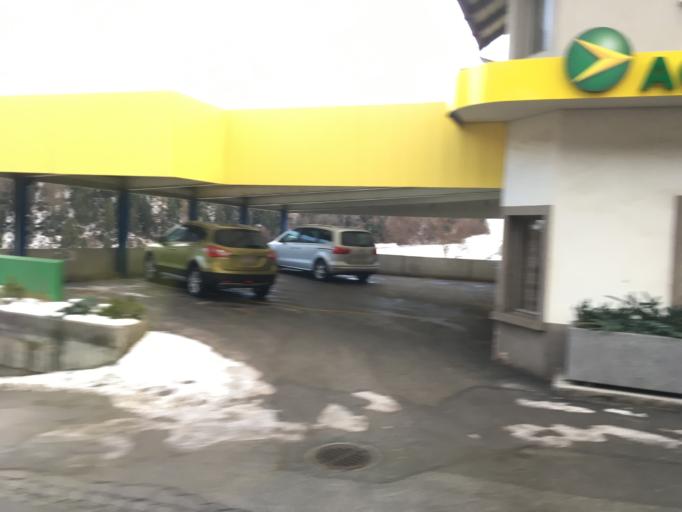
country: CH
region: Grisons
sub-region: Albula District
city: Tiefencastel
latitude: 46.6641
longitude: 9.5718
